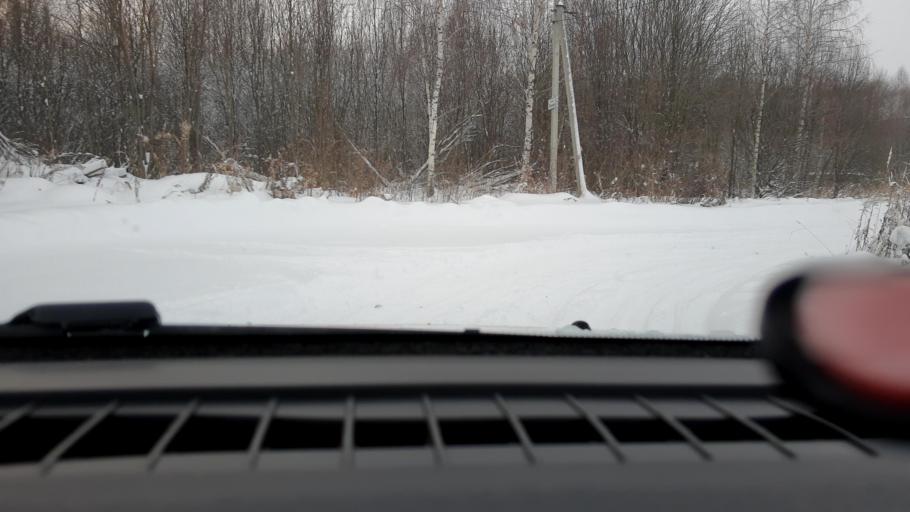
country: RU
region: Nizjnij Novgorod
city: Afonino
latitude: 56.1314
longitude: 43.9813
